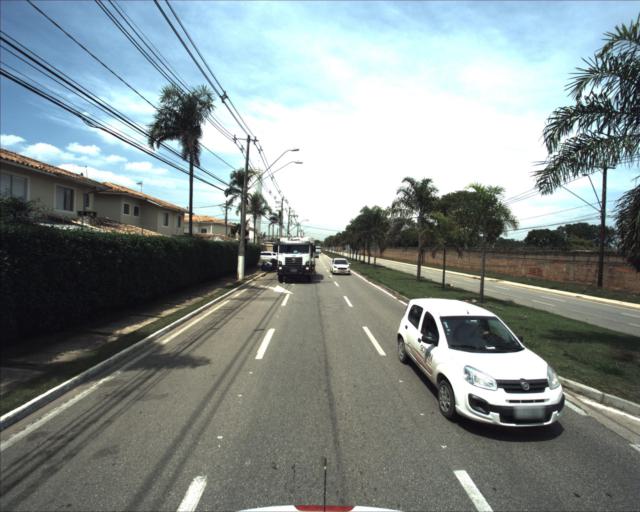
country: BR
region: Sao Paulo
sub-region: Votorantim
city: Votorantim
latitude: -23.5468
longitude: -47.4797
